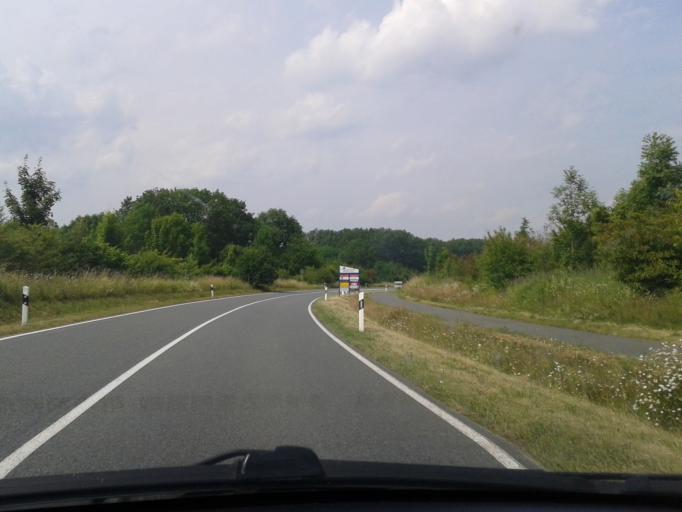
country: DE
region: North Rhine-Westphalia
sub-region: Regierungsbezirk Detmold
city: Paderborn
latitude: 51.7010
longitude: 8.7108
